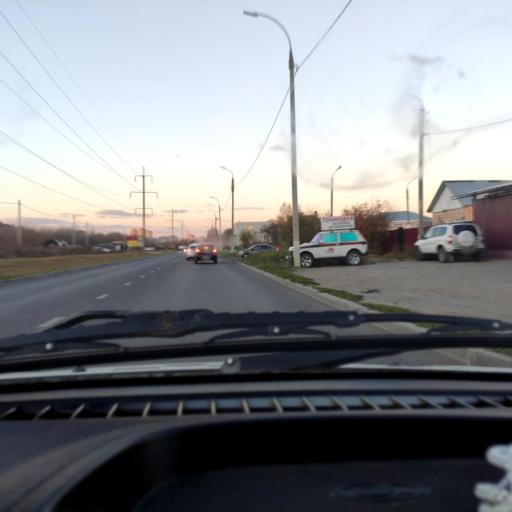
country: RU
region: Samara
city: Tol'yatti
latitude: 53.5184
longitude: 49.3957
